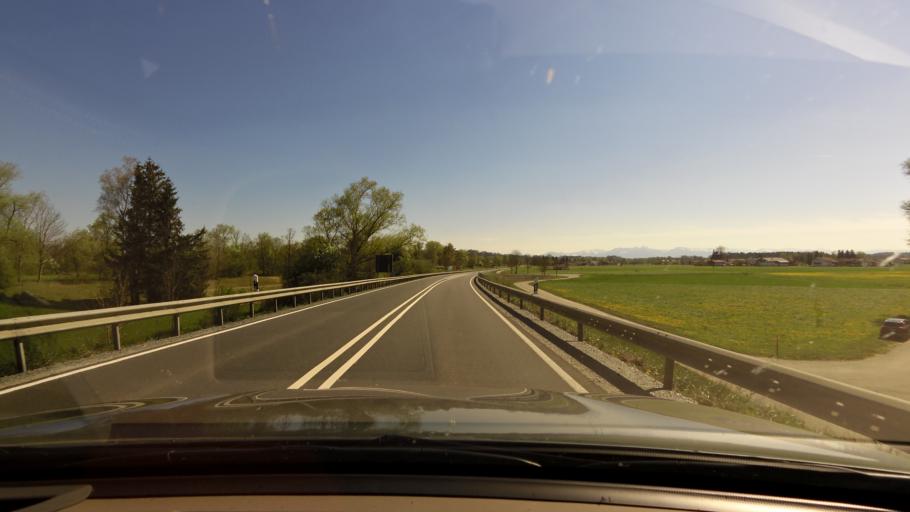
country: DE
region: Bavaria
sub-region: Upper Bavaria
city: Griesstatt
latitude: 48.0211
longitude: 12.1731
